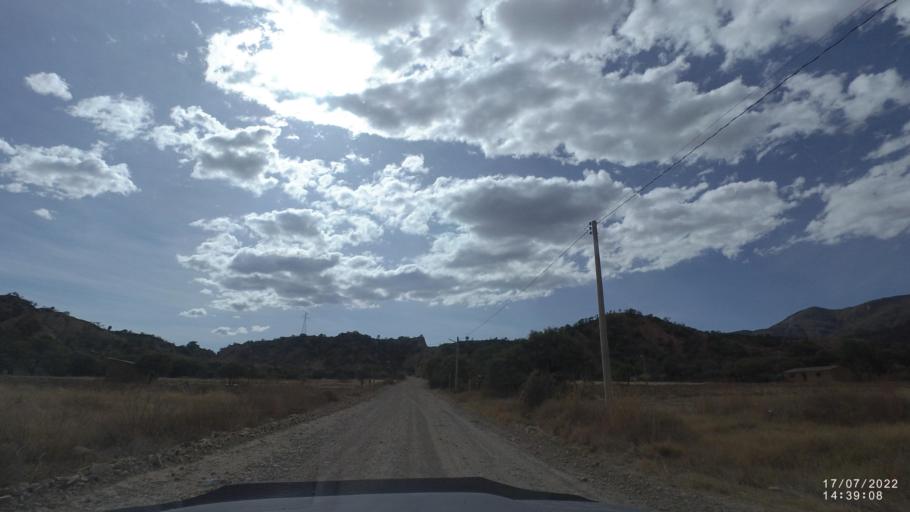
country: BO
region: Cochabamba
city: Capinota
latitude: -17.6402
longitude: -66.2488
